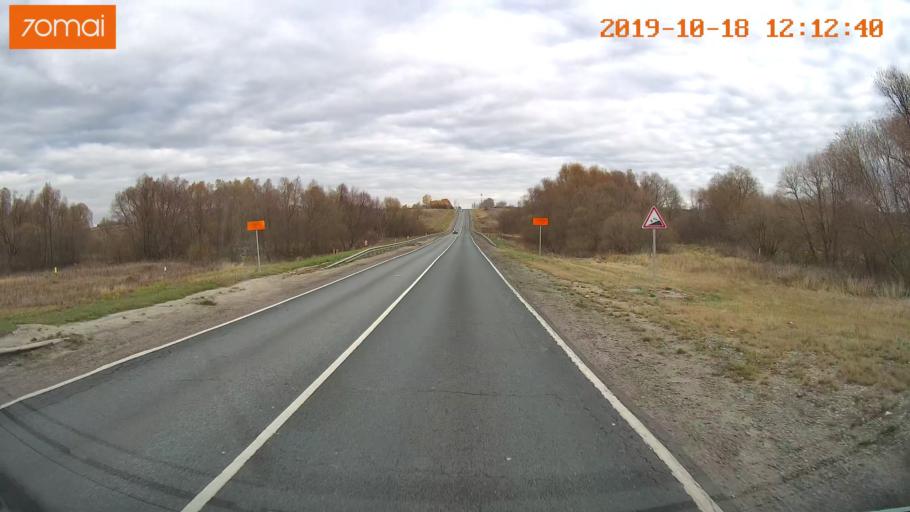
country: RU
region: Rjazan
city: Zakharovo
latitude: 54.4140
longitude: 39.3608
